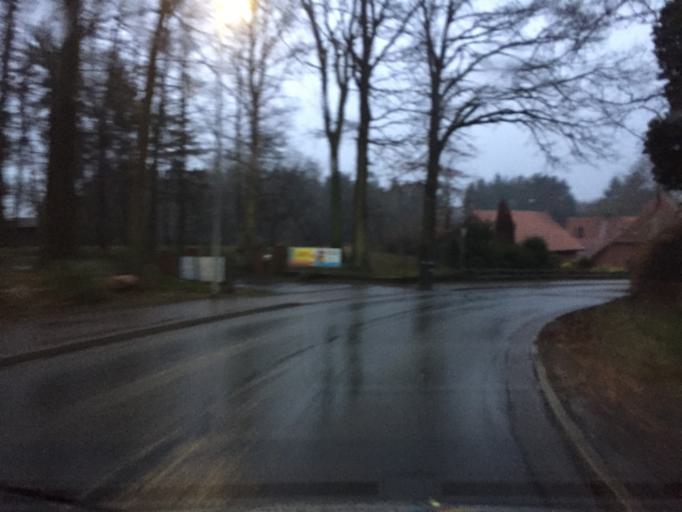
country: DE
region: Lower Saxony
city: Sudwalde
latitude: 52.8419
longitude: 8.8460
